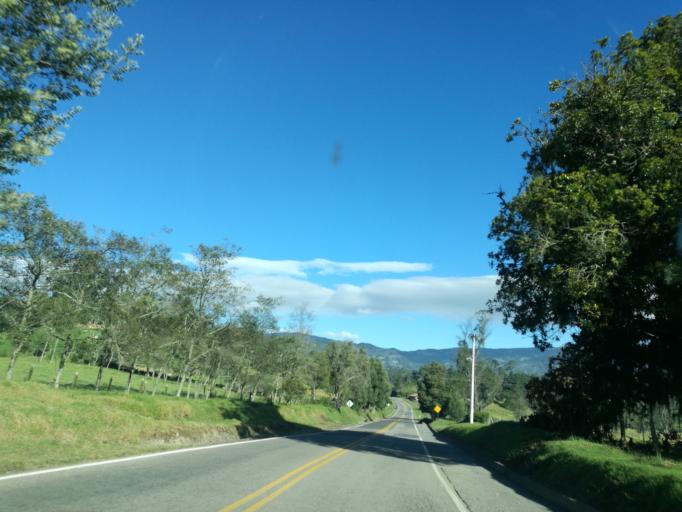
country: CO
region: Boyaca
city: Chiquinquira
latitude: 5.6210
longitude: -73.7821
